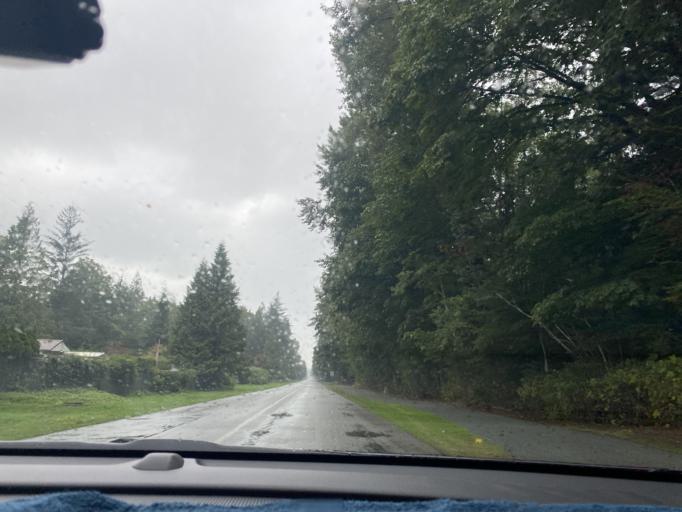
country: CA
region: British Columbia
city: Agassiz
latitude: 49.2814
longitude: -121.7775
